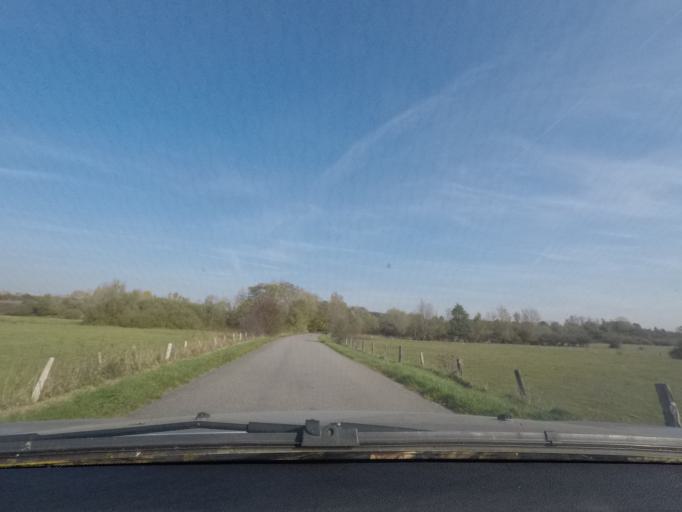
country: BE
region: Wallonia
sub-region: Province du Luxembourg
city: Tintigny
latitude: 49.6974
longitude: 5.4926
